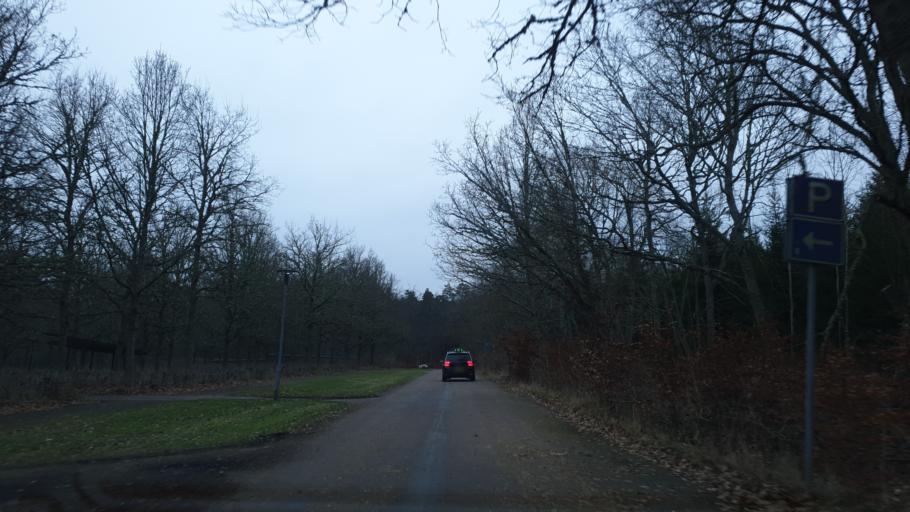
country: SE
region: Blekinge
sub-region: Karlskrona Kommun
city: Rodeby
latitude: 56.2128
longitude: 15.6829
